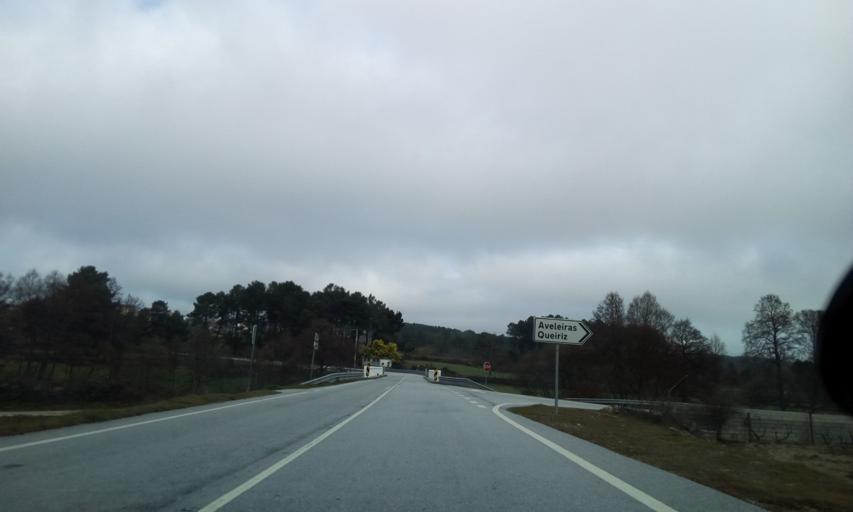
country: PT
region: Guarda
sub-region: Fornos de Algodres
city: Fornos de Algodres
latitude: 40.7177
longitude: -7.4878
